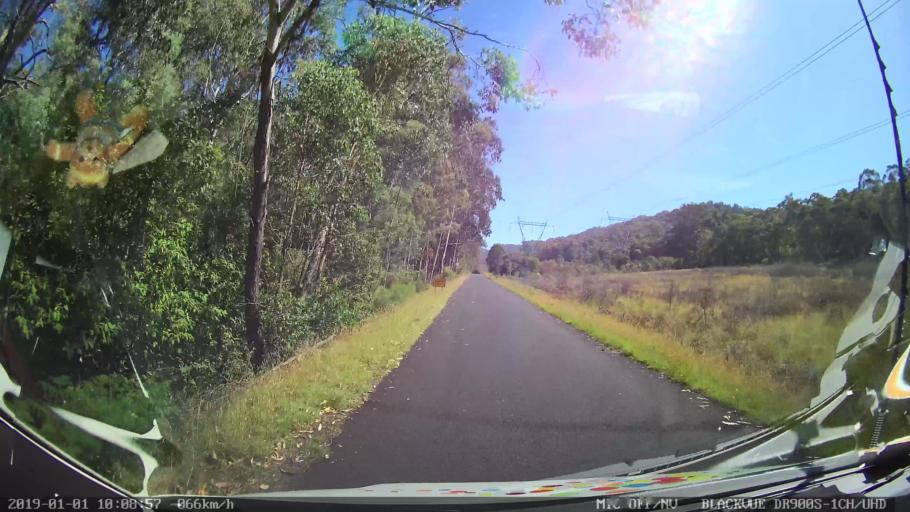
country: AU
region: New South Wales
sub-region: Snowy River
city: Jindabyne
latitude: -36.1543
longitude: 148.1580
